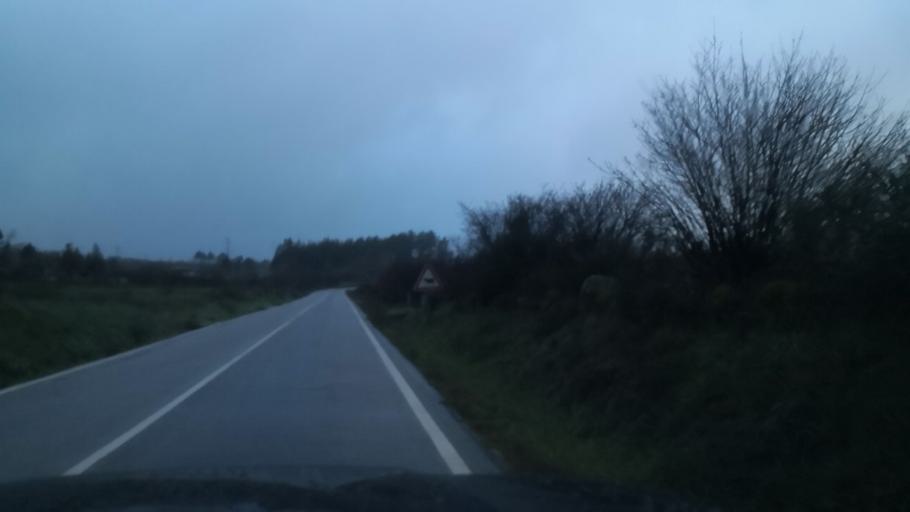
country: PT
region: Vila Real
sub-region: Murca
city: Murca
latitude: 41.4330
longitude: -7.5432
